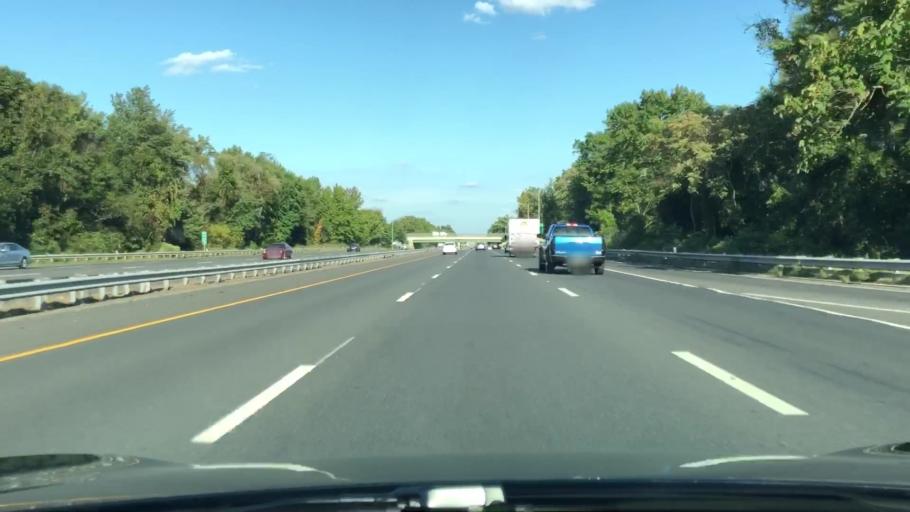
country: US
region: New Jersey
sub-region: Gloucester County
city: Gibbstown
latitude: 39.8106
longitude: -75.2771
